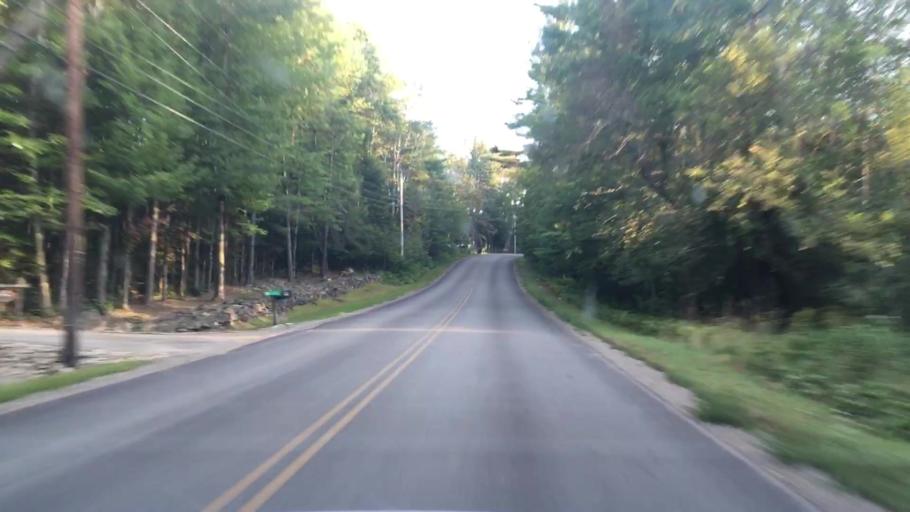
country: US
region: Maine
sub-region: Penobscot County
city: Hampden
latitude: 44.7131
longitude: -68.8868
